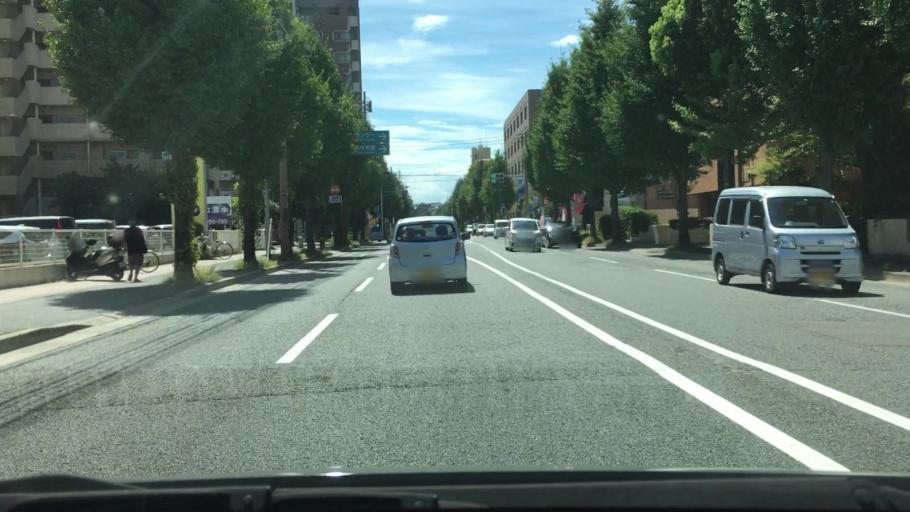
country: JP
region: Fukuoka
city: Fukuoka-shi
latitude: 33.5687
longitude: 130.4257
